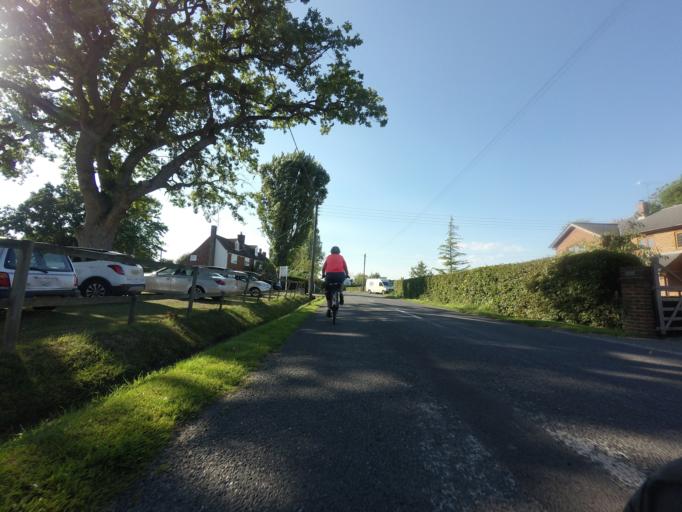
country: GB
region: England
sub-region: Kent
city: Tenterden
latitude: 51.0600
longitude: 0.6917
